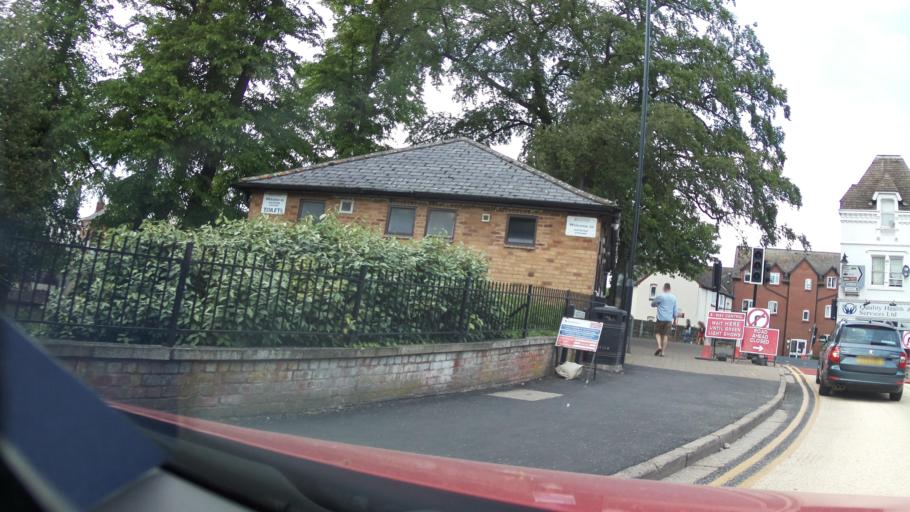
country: GB
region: England
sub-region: Worcestershire
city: Evesham
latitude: 52.0909
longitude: -1.9422
